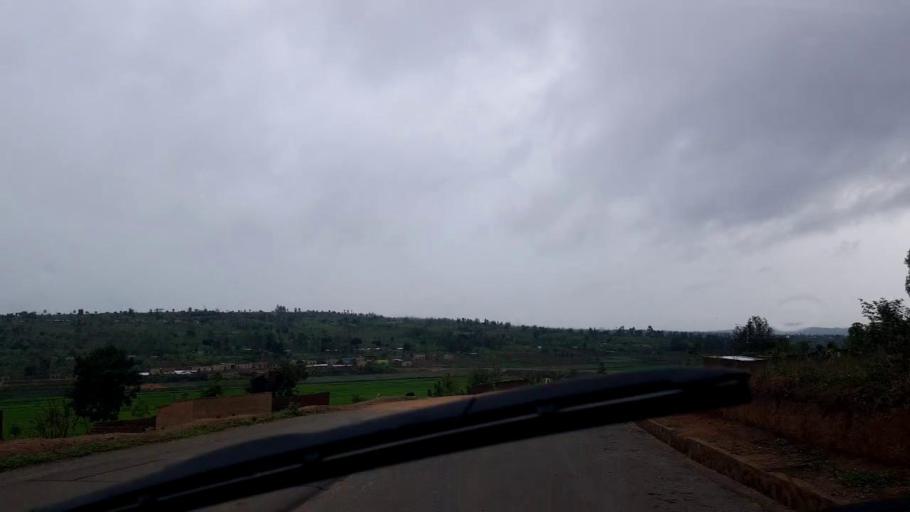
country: RW
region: Northern Province
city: Byumba
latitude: -1.4246
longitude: 30.2720
